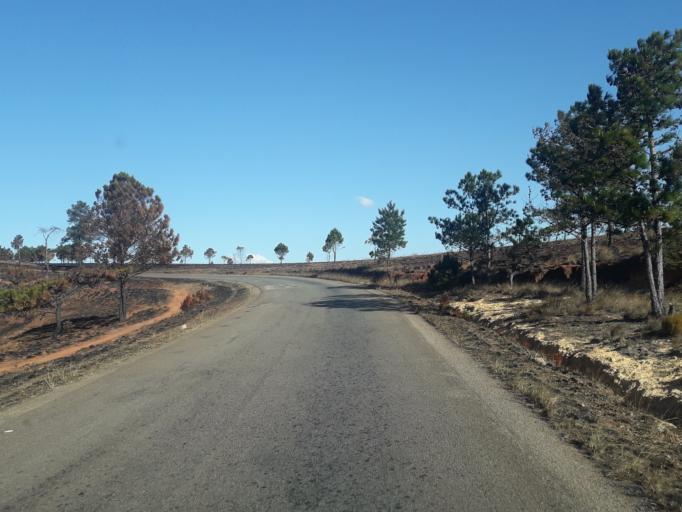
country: MG
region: Analamanga
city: Ankazobe
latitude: -17.8819
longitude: 47.0785
